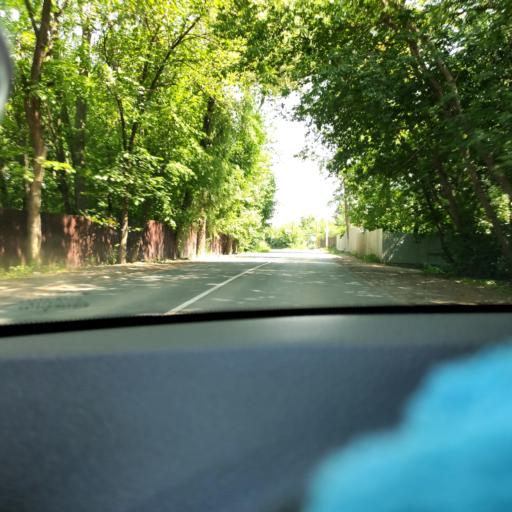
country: RU
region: Samara
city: Novokuybyshevsk
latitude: 53.1538
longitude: 49.9630
